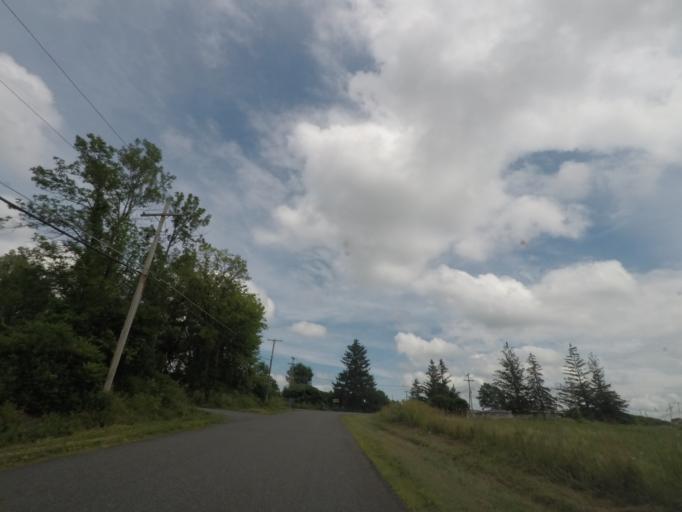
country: US
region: New York
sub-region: Saratoga County
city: Stillwater
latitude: 43.0093
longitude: -73.6869
